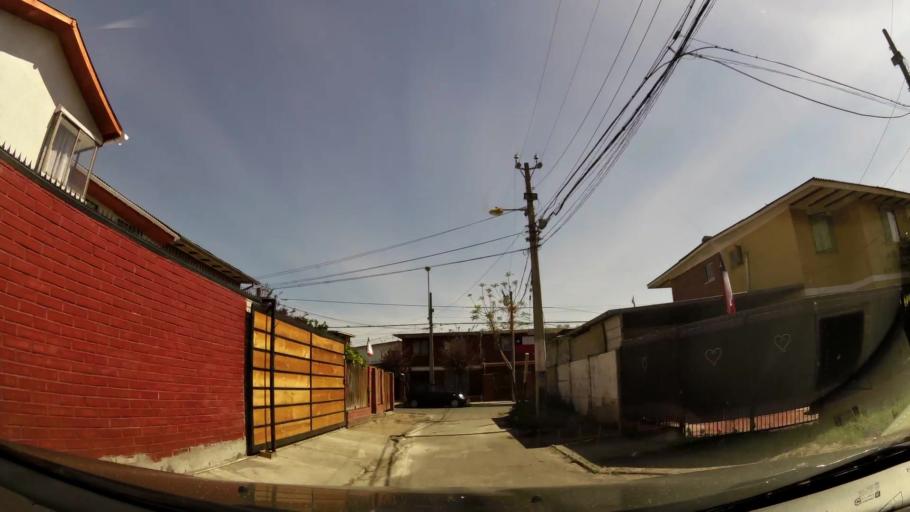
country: CL
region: Santiago Metropolitan
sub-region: Provincia de Cordillera
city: Puente Alto
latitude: -33.5702
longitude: -70.5690
